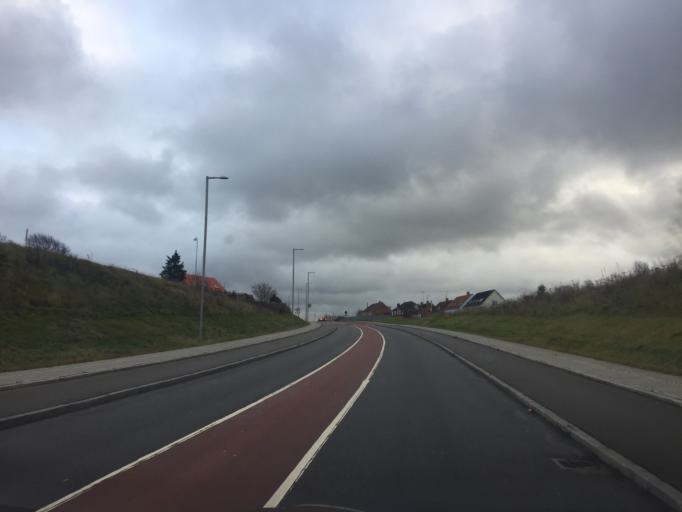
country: DK
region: Zealand
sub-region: Holbaek Kommune
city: Tollose
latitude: 55.6146
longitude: 11.7704
